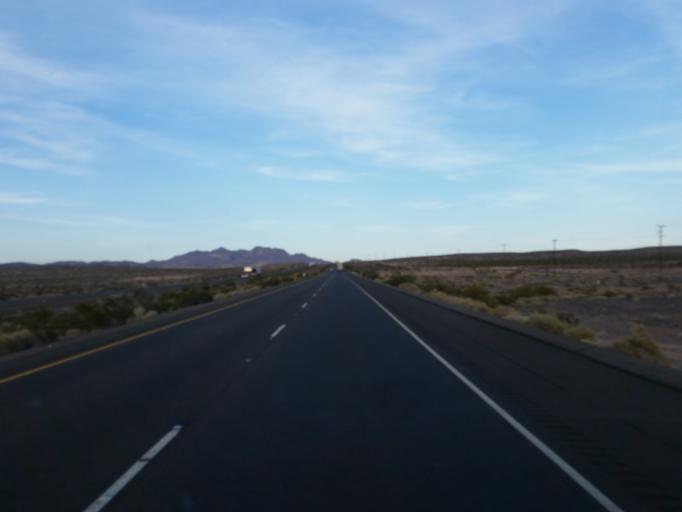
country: US
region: California
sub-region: San Bernardino County
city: Fort Irwin
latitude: 34.7861
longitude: -116.4372
